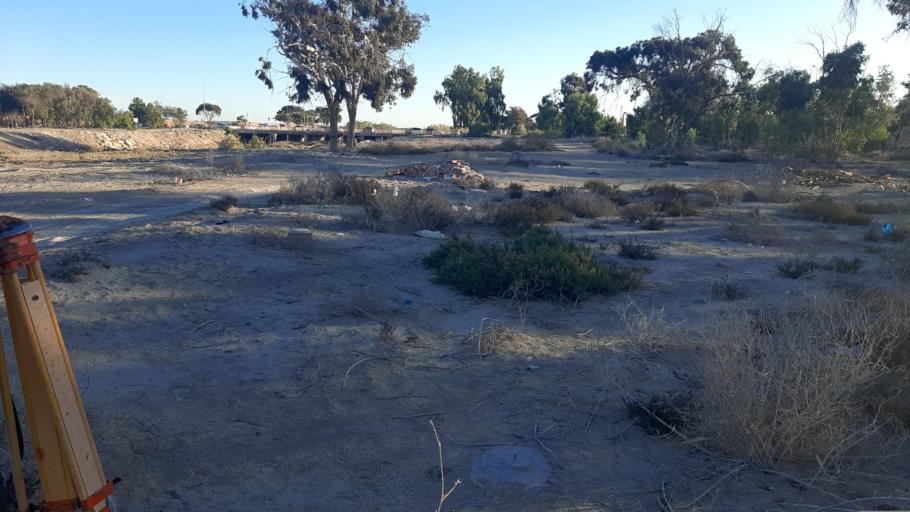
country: TN
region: Qabis
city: Gabes
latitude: 33.8771
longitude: 10.1089
